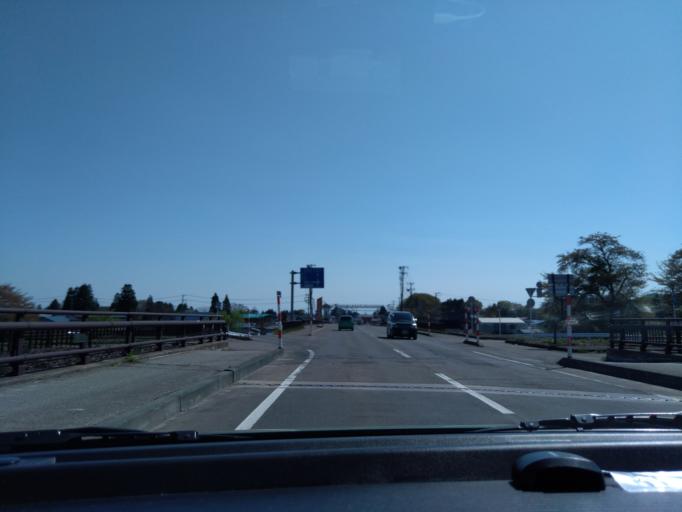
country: JP
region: Akita
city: Kakunodatemachi
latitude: 39.5790
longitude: 140.5671
